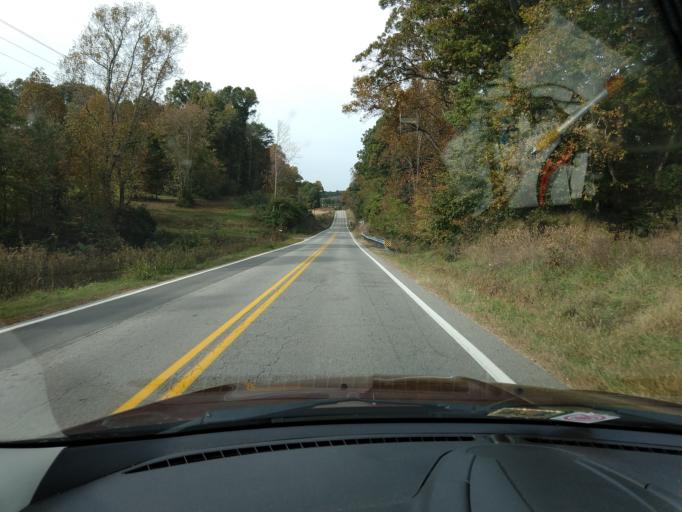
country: US
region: Virginia
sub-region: Pittsylvania County
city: Gretna
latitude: 36.9452
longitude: -79.4754
